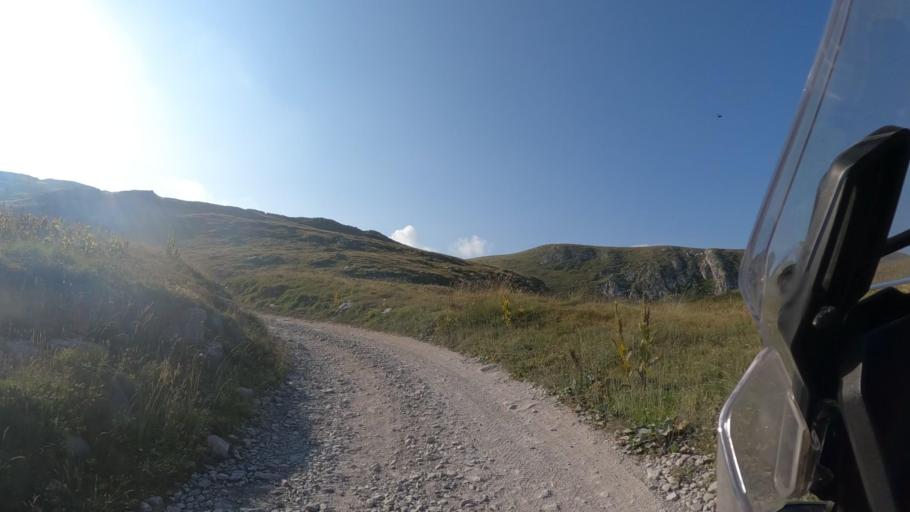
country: IT
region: Piedmont
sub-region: Provincia di Cuneo
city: Limone Piemonte
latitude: 44.1722
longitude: 7.6459
